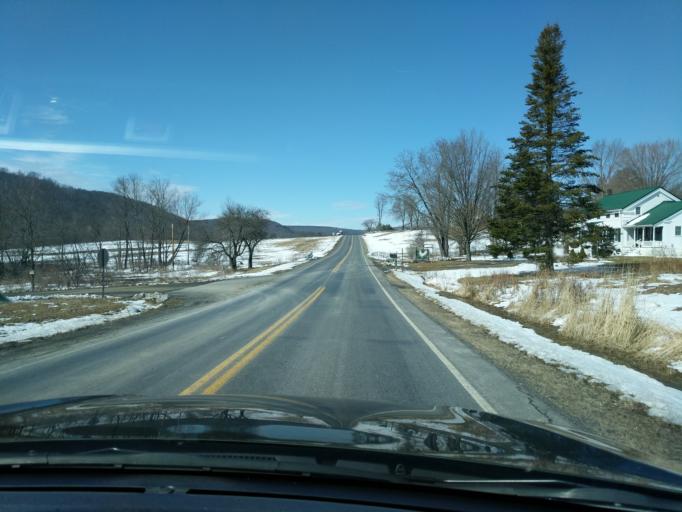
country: US
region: New York
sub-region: Tompkins County
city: Dryden
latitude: 42.3111
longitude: -76.2650
